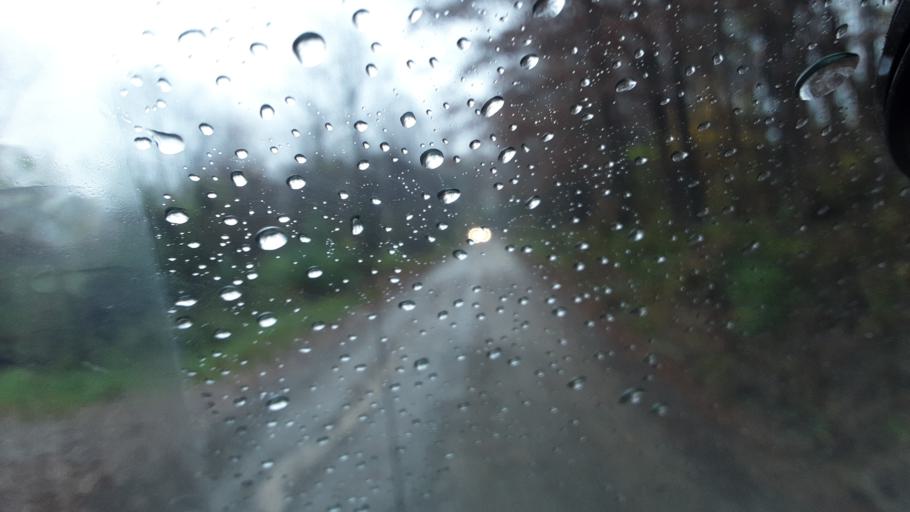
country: US
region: Ohio
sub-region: Vinton County
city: McArthur
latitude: 39.2251
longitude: -82.4622
